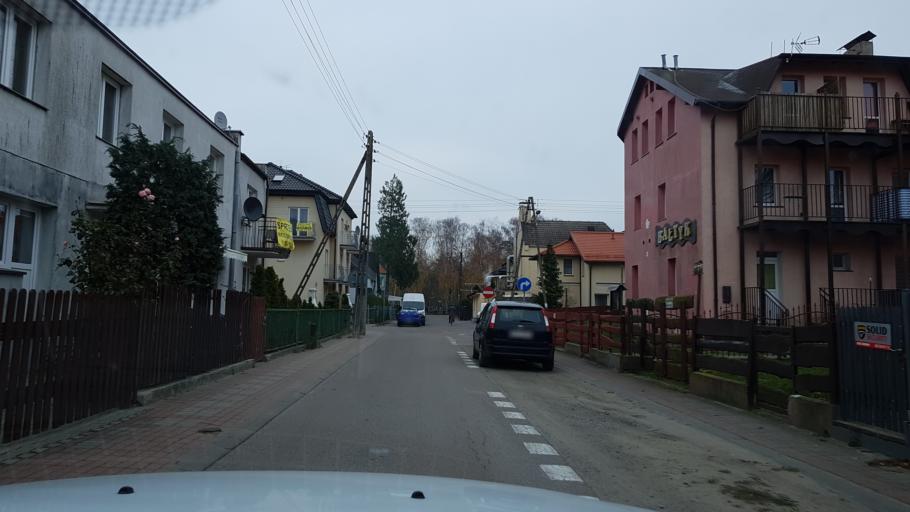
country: PL
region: West Pomeranian Voivodeship
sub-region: Powiat kamienski
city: Dziwnow
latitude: 54.0061
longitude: 14.6946
